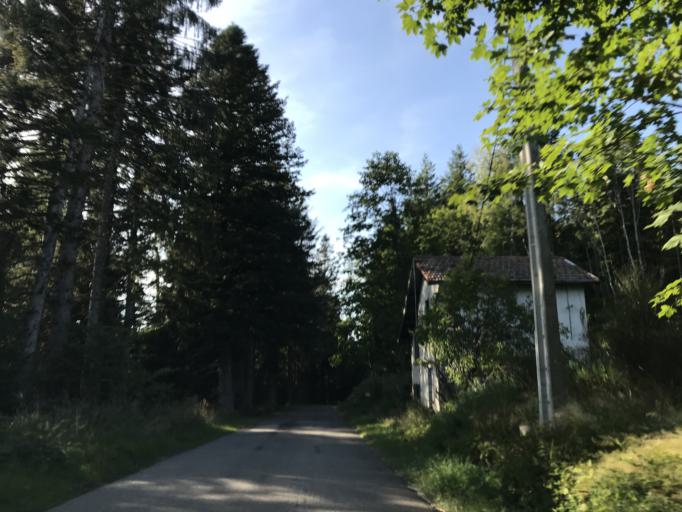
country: FR
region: Auvergne
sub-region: Departement du Puy-de-Dome
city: Job
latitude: 45.6720
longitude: 3.7382
